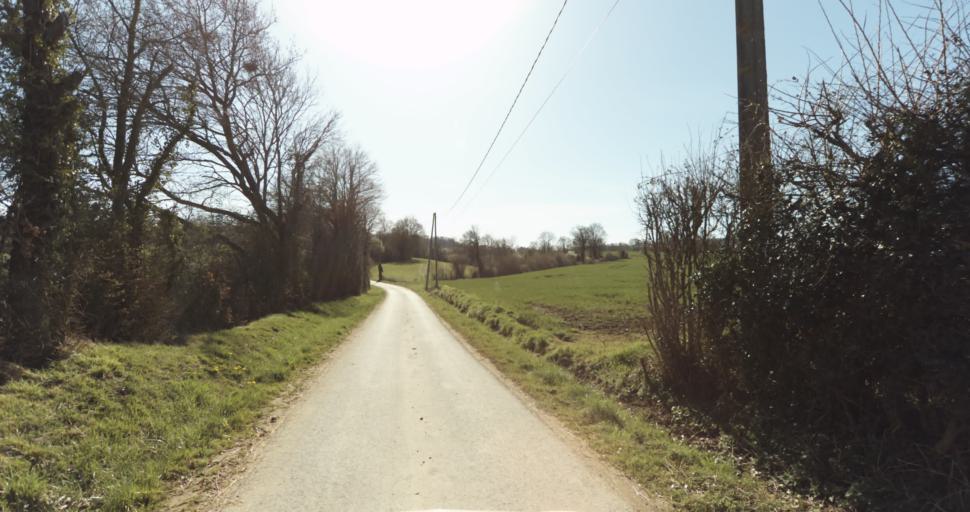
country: FR
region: Lower Normandy
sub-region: Departement de l'Orne
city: Trun
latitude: 48.9148
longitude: 0.0430
